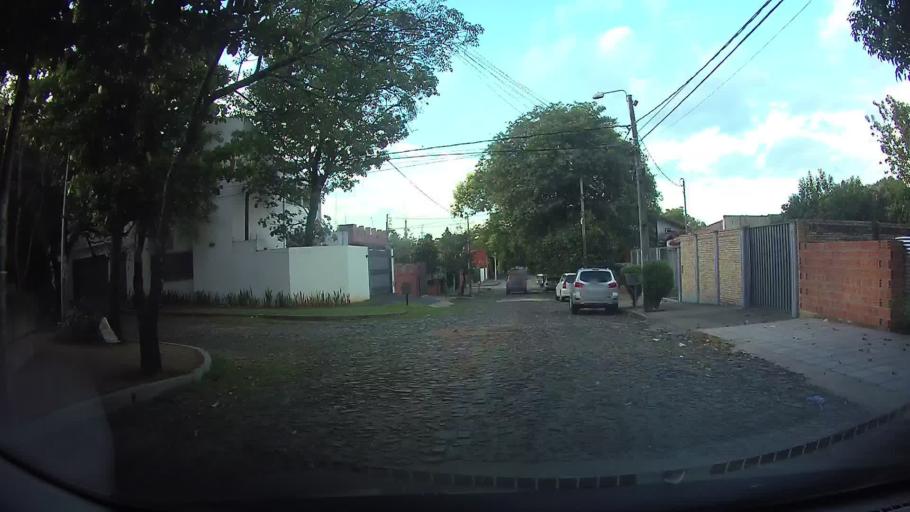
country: PY
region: Asuncion
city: Asuncion
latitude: -25.2719
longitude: -57.5950
